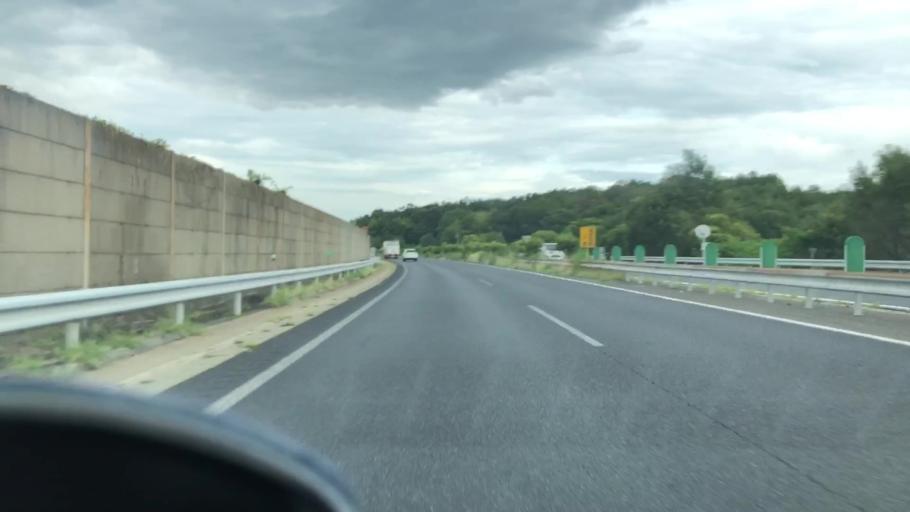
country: JP
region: Hyogo
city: Yashiro
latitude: 34.9184
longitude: 135.0112
